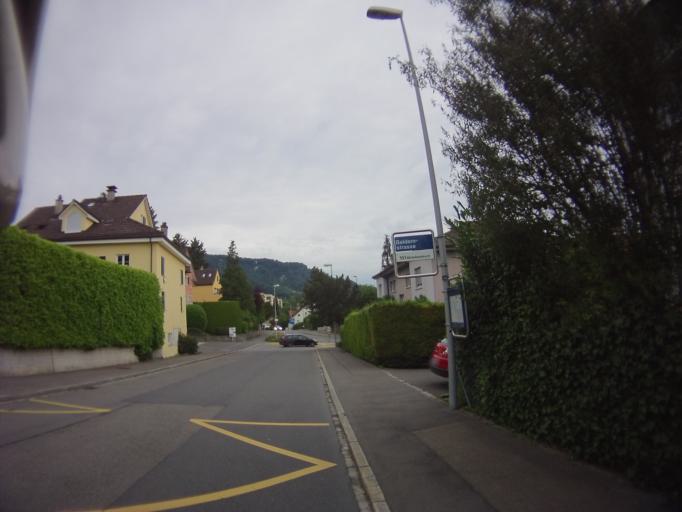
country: CH
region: Zurich
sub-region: Bezirk Horgen
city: Adliswil / Oberleimbach
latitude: 47.3206
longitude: 8.5157
